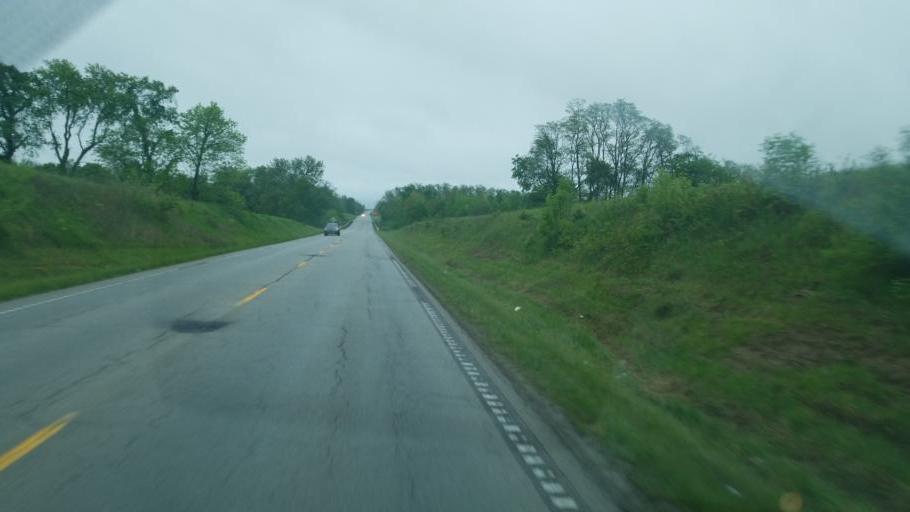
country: US
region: Ohio
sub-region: Highland County
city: Leesburg
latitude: 39.2956
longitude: -83.5867
